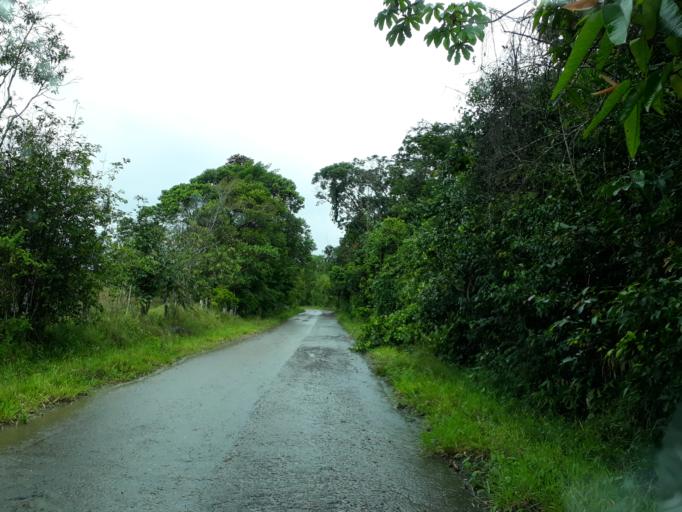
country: CO
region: Boyaca
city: Santa Maria
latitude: 4.6898
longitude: -73.3080
